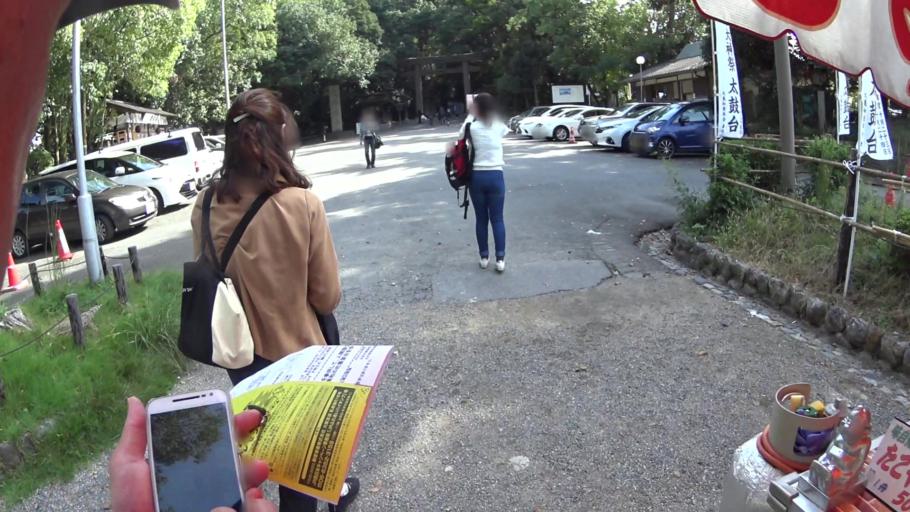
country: JP
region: Nara
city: Sakurai
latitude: 34.5293
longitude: 135.8489
